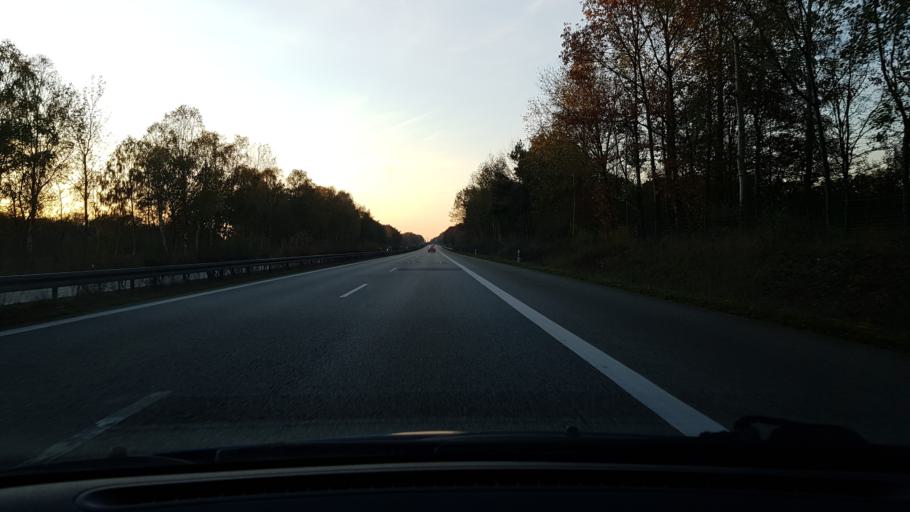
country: DE
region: Mecklenburg-Vorpommern
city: Wittenburg
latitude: 53.5069
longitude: 11.0037
